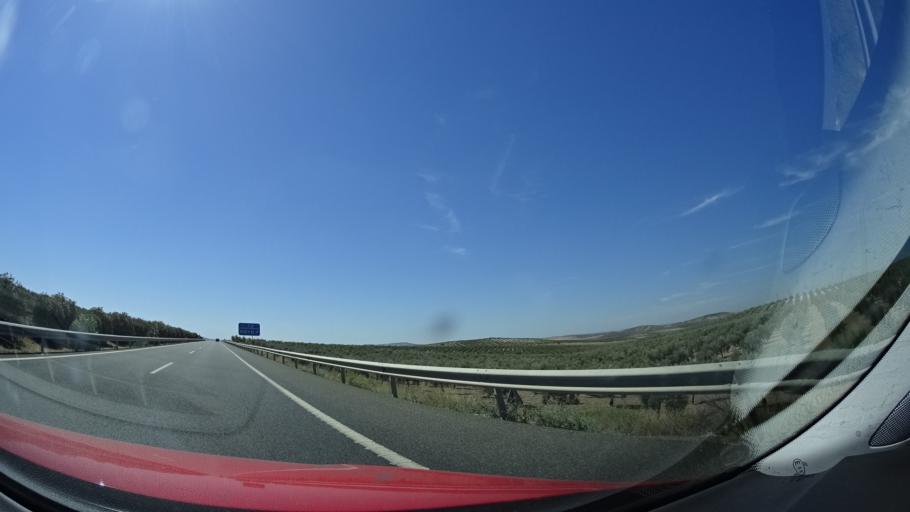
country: ES
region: Andalusia
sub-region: Provincia de Sevilla
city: Gilena
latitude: 37.2710
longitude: -4.9494
